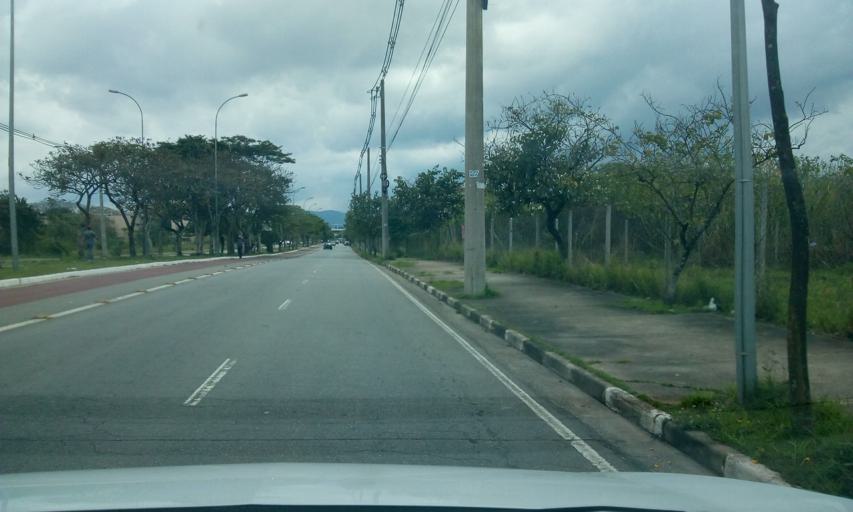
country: BR
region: Sao Paulo
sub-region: Guarulhos
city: Guarulhos
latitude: -23.4546
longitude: -46.4940
